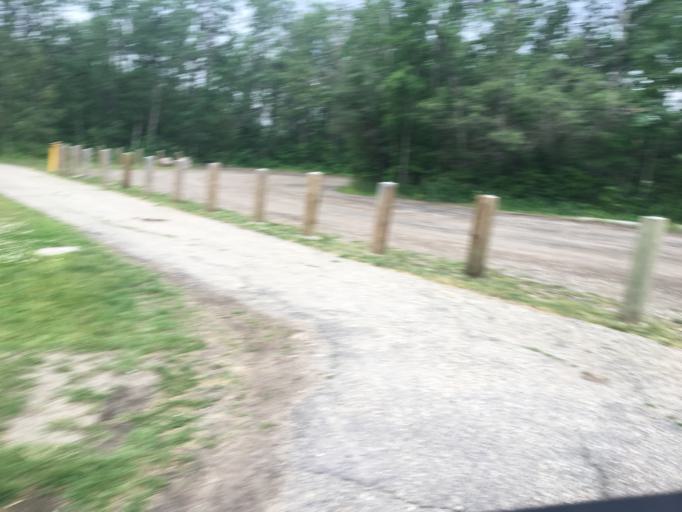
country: CA
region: Alberta
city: Grande Prairie
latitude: 55.1341
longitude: -118.7940
